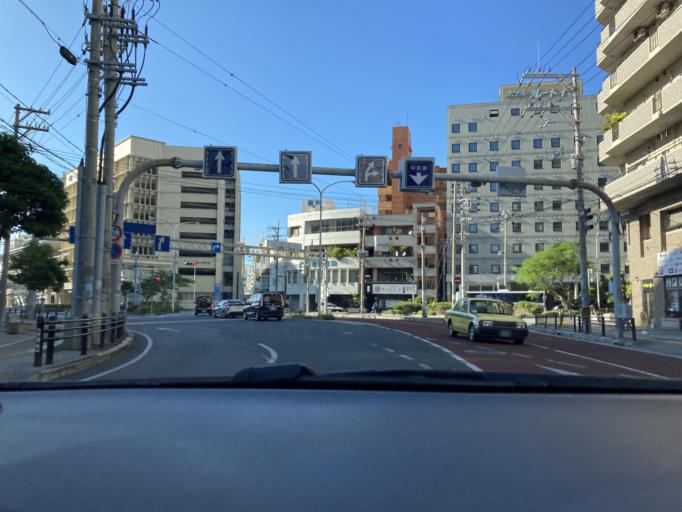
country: JP
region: Okinawa
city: Naha-shi
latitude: 26.2098
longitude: 127.6784
